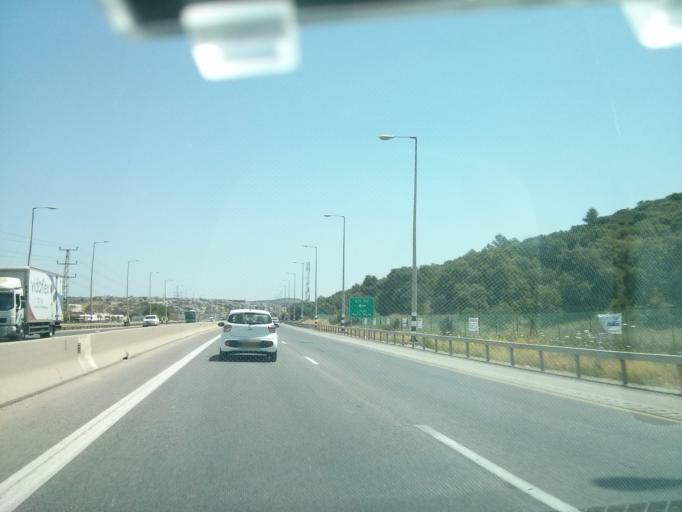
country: PS
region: West Bank
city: Barta`ah ash Sharqiyah
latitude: 32.4951
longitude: 35.0597
